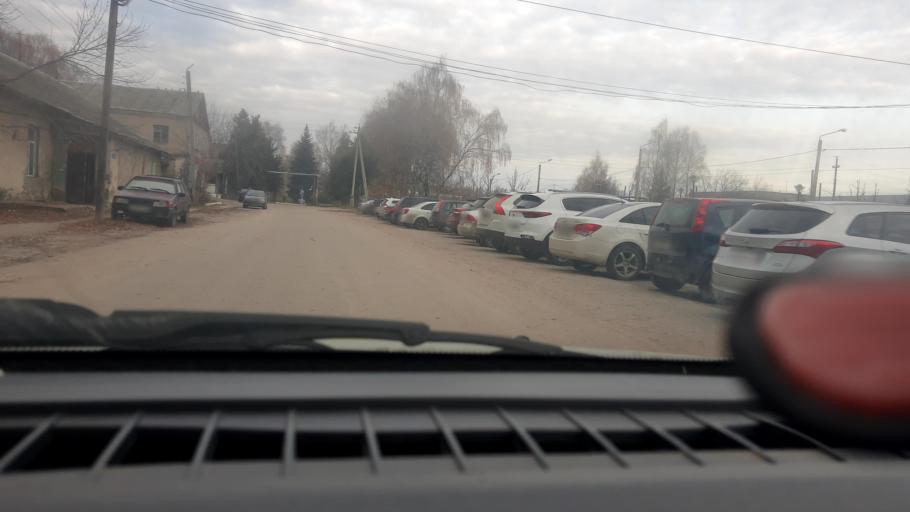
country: RU
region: Nizjnij Novgorod
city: Afonino
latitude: 56.2074
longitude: 44.1072
